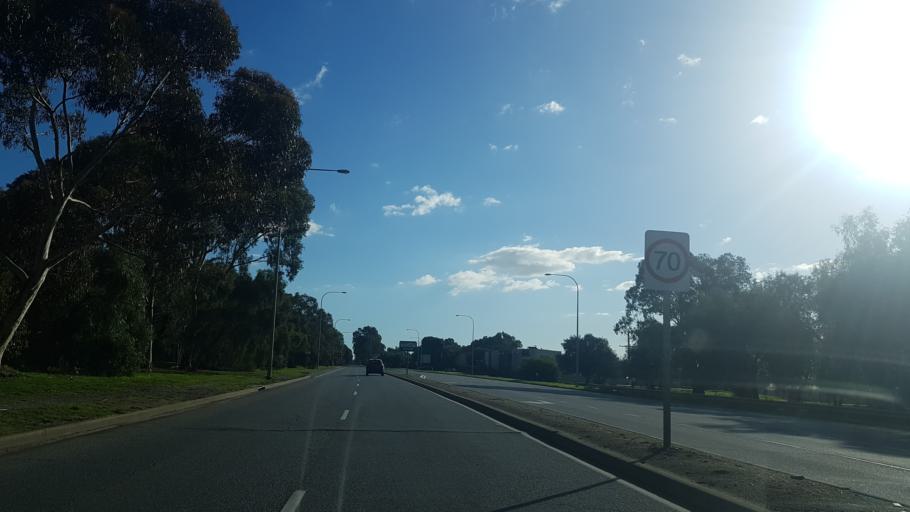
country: AU
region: South Australia
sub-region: Salisbury
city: Ingle Farm
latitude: -34.8247
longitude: 138.6170
